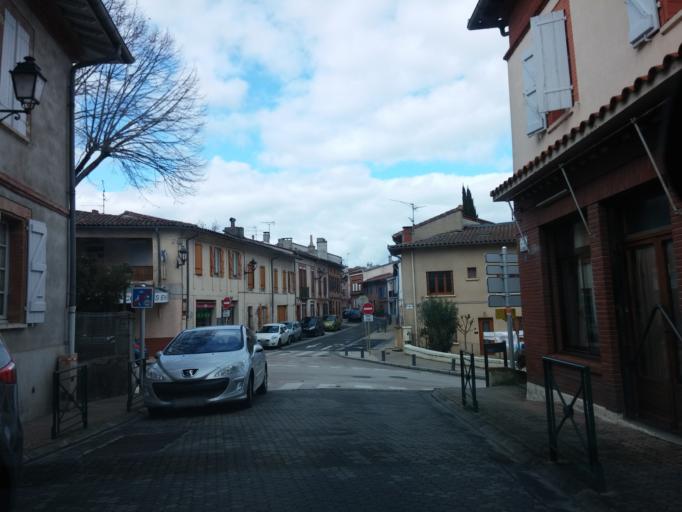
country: FR
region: Midi-Pyrenees
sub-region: Departement de la Haute-Garonne
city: Blagnac
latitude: 43.6346
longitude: 1.3998
